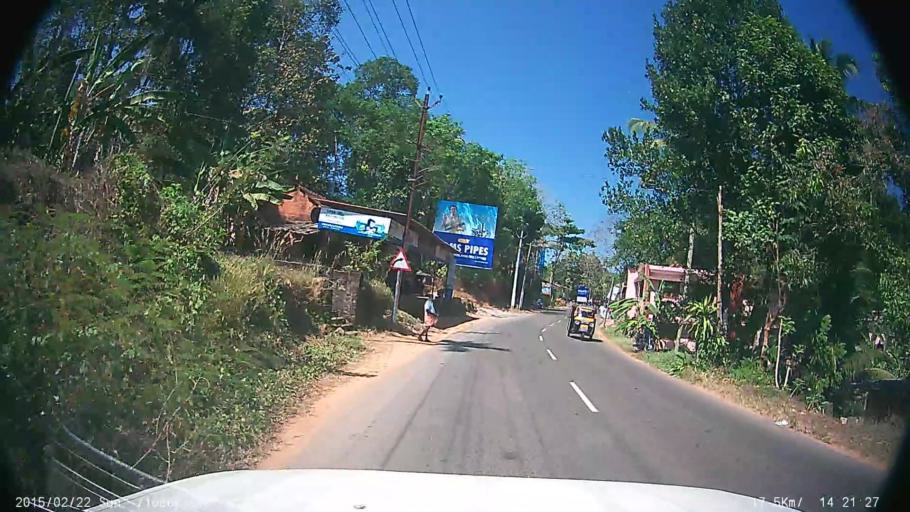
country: IN
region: Kerala
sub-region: Kottayam
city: Lalam
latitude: 9.5638
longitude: 76.6992
